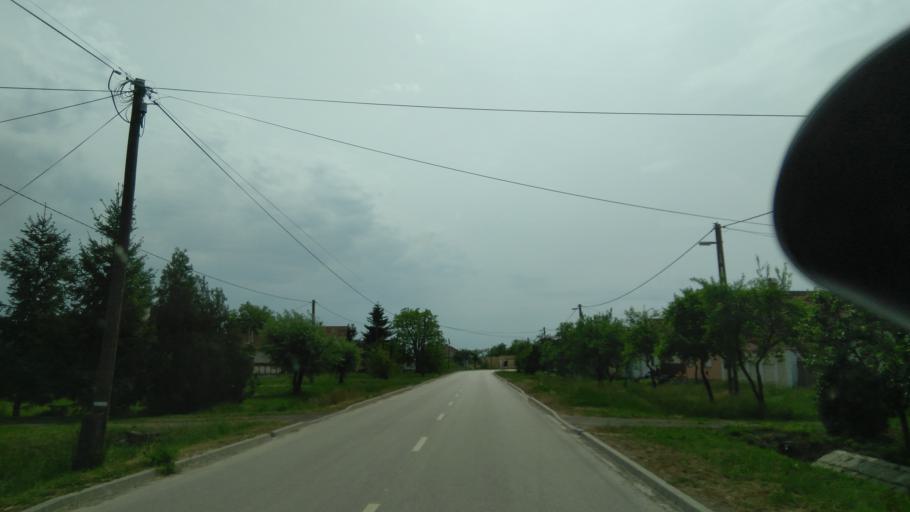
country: HU
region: Bekes
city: Mehkerek
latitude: 46.8675
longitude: 21.5205
